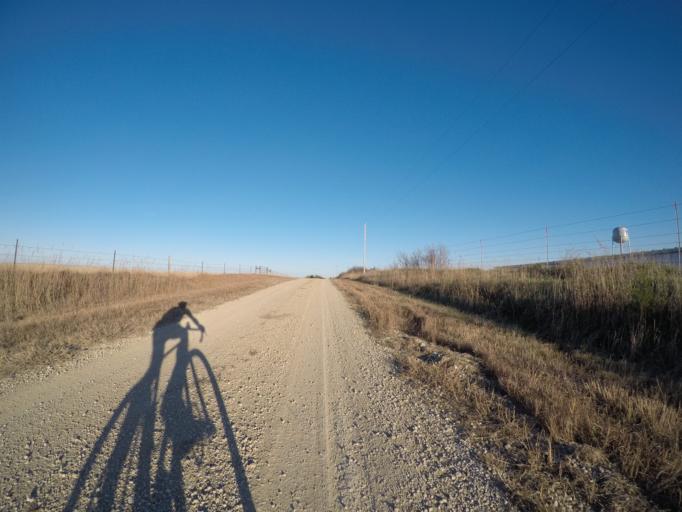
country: US
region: Kansas
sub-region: Riley County
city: Manhattan
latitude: 39.2544
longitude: -96.6673
